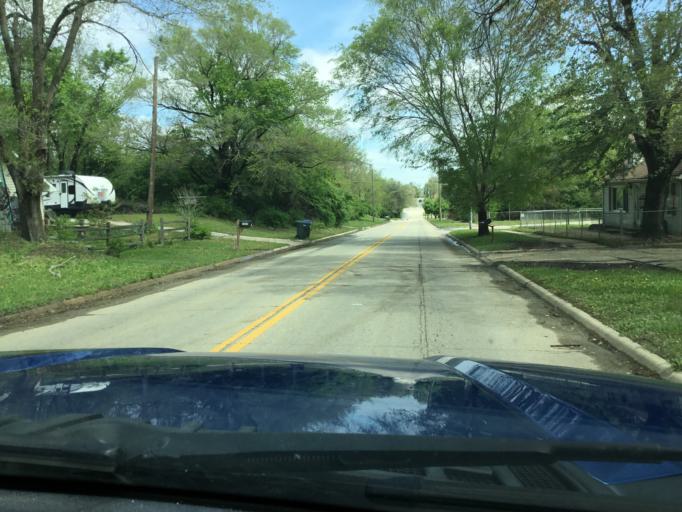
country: US
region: Kansas
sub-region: Shawnee County
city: Topeka
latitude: 39.0265
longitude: -95.6606
